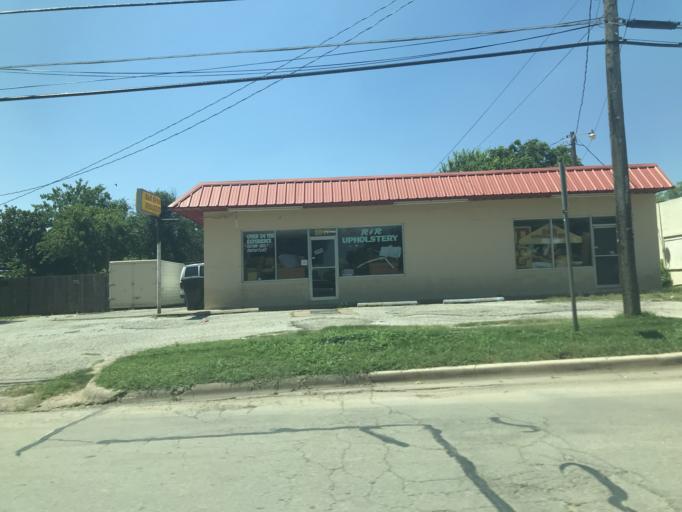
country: US
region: Texas
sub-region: Taylor County
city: Abilene
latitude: 32.4632
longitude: -99.7519
